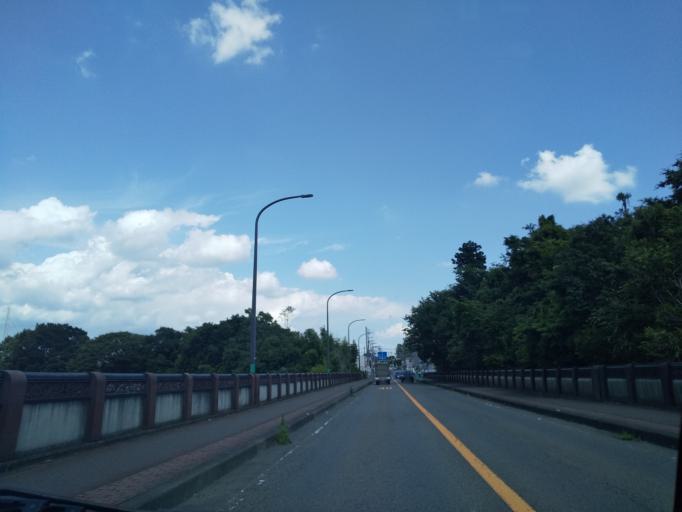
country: JP
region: Kanagawa
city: Zama
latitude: 35.4910
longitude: 139.4128
